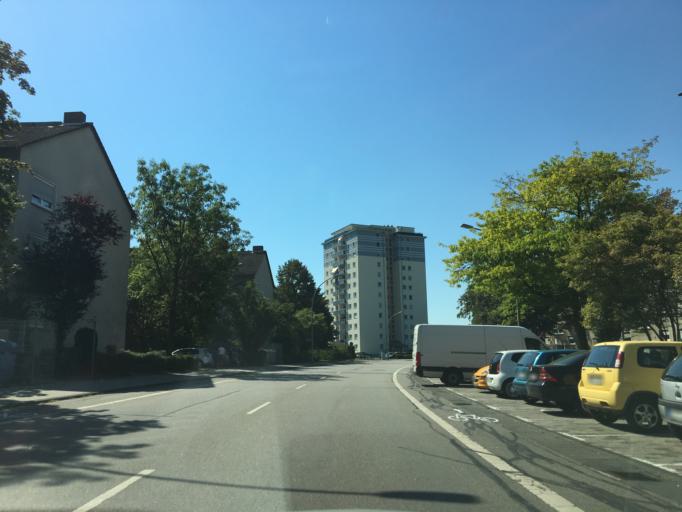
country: DE
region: Hesse
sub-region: Regierungsbezirk Darmstadt
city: Russelsheim
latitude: 49.9842
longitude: 8.4497
